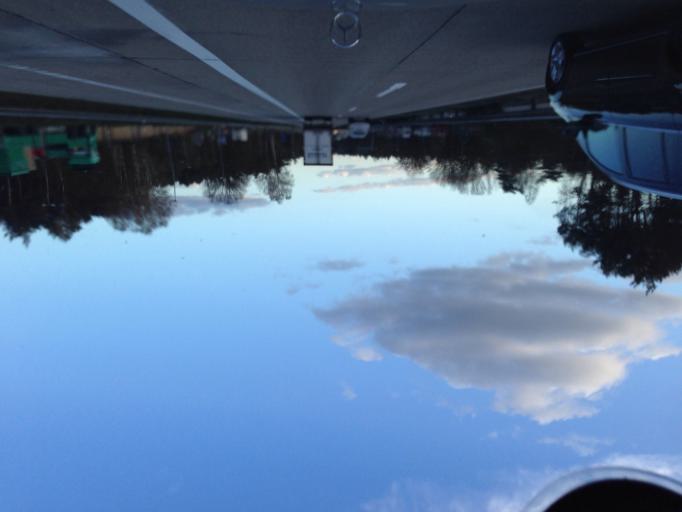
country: DE
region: Lower Saxony
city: Bad Fallingbostel
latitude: 52.8085
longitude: 9.6794
